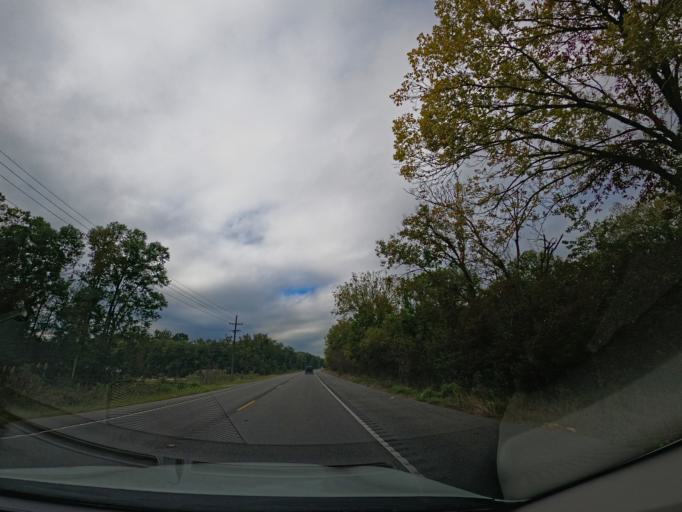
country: US
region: Louisiana
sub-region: Saint Mary Parish
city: Amelia
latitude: 29.6797
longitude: -91.0084
